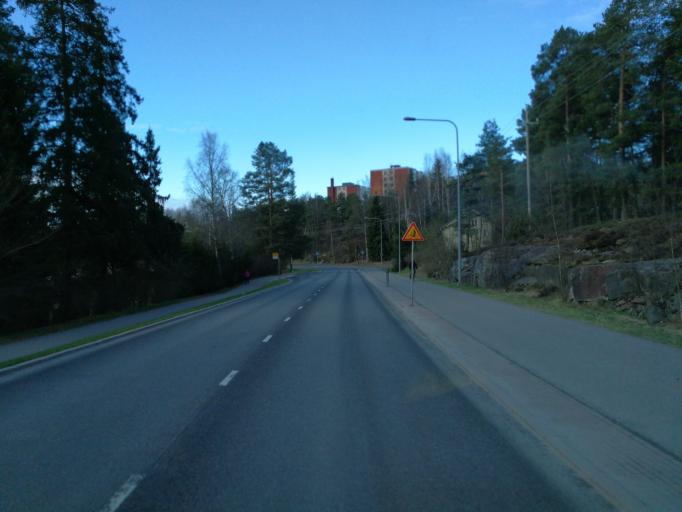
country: FI
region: Varsinais-Suomi
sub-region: Turku
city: Turku
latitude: 60.4258
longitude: 22.2921
